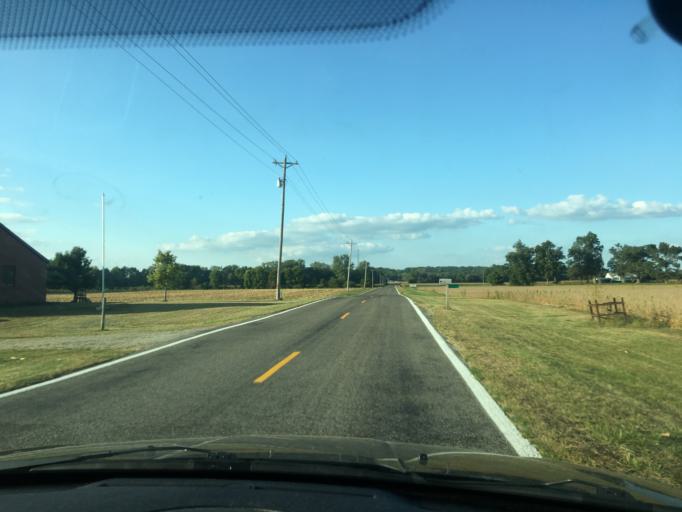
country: US
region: Ohio
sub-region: Logan County
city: West Liberty
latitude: 40.2124
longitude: -83.7788
